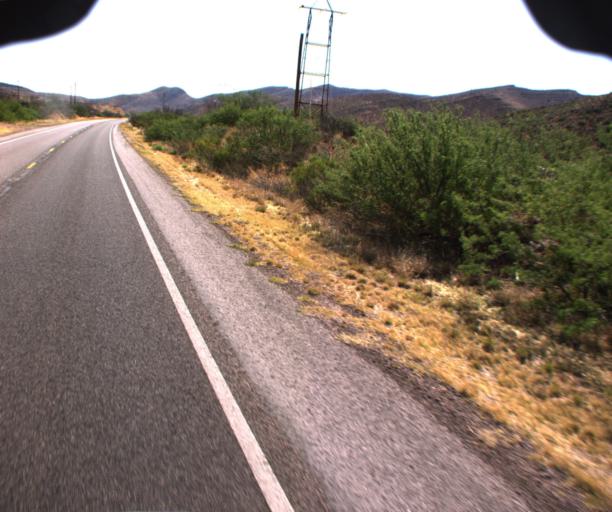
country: US
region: Arizona
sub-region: Cochise County
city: Bisbee
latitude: 31.4294
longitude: -109.8737
